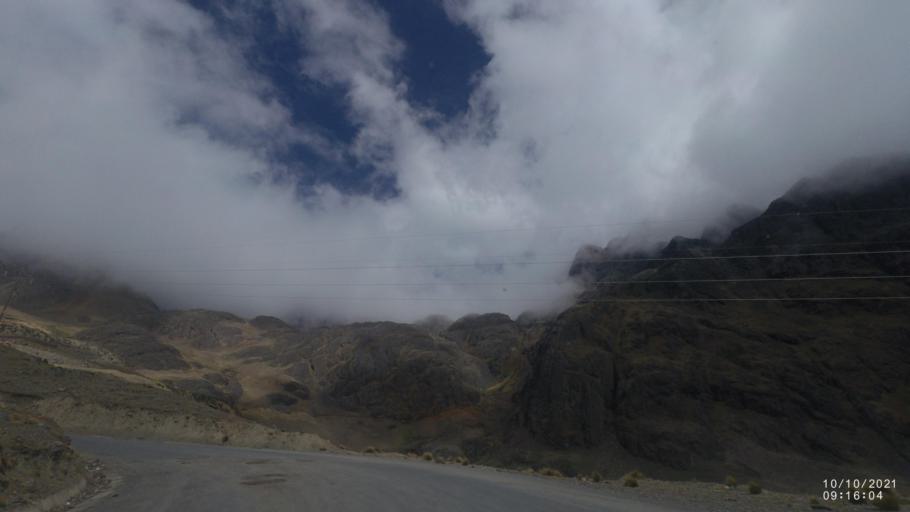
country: BO
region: La Paz
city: Quime
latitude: -17.0465
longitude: -67.2940
